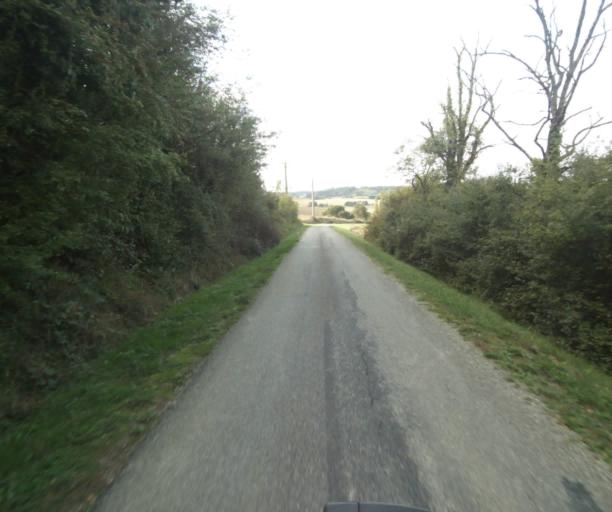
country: FR
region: Midi-Pyrenees
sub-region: Departement de la Haute-Garonne
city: Launac
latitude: 43.8165
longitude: 1.0926
